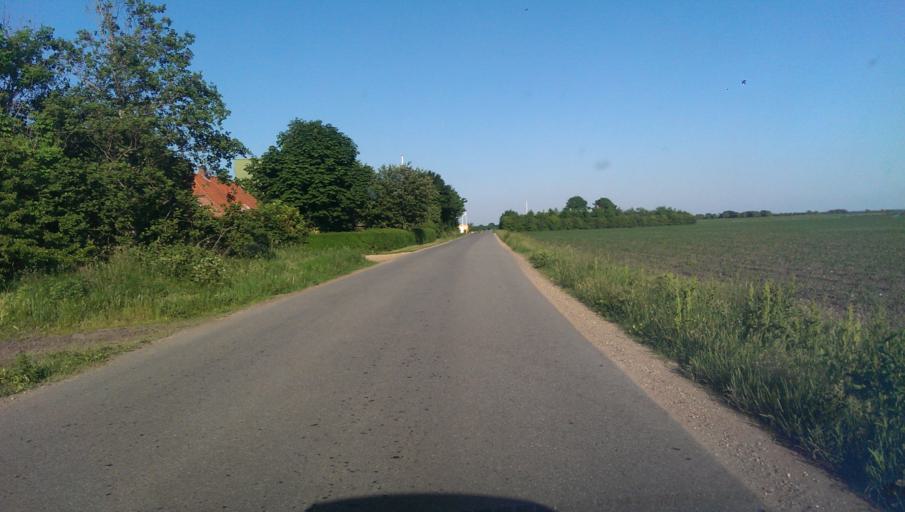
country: DK
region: South Denmark
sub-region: Esbjerg Kommune
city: Bramming
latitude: 55.5484
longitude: 8.6518
